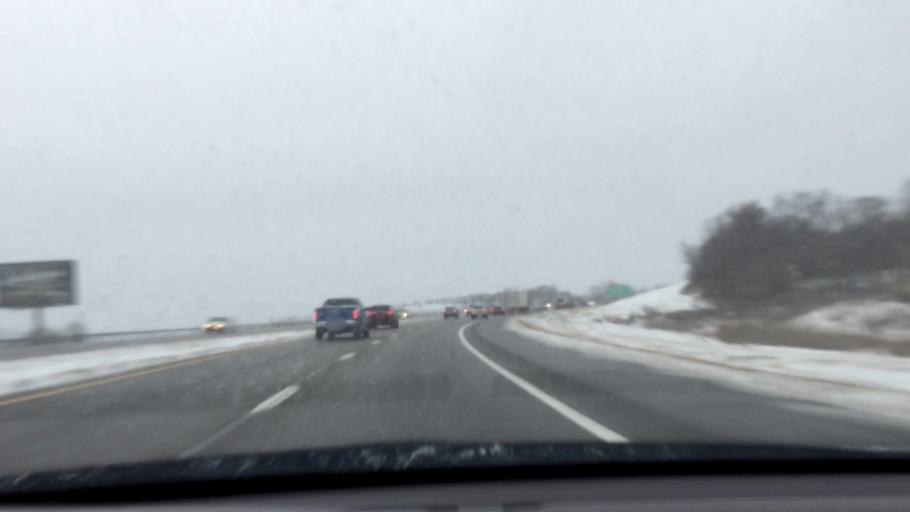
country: US
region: Pennsylvania
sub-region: Washington County
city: Canonsburg
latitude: 40.2878
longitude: -80.1688
